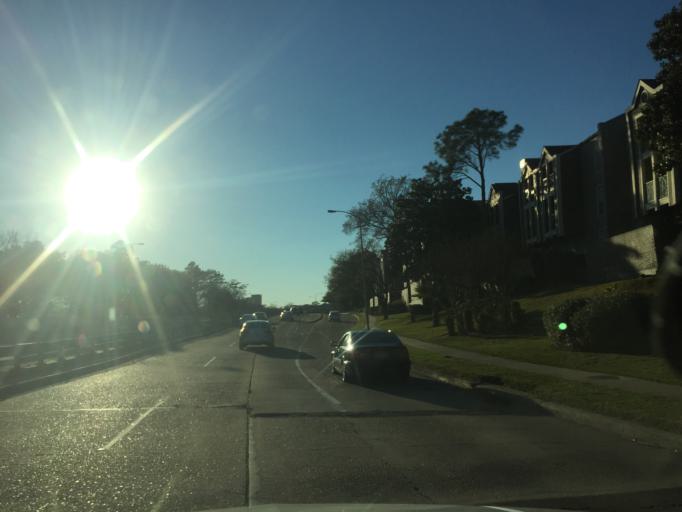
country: US
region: Texas
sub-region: Harris County
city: Houston
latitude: 29.7618
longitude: -95.4044
